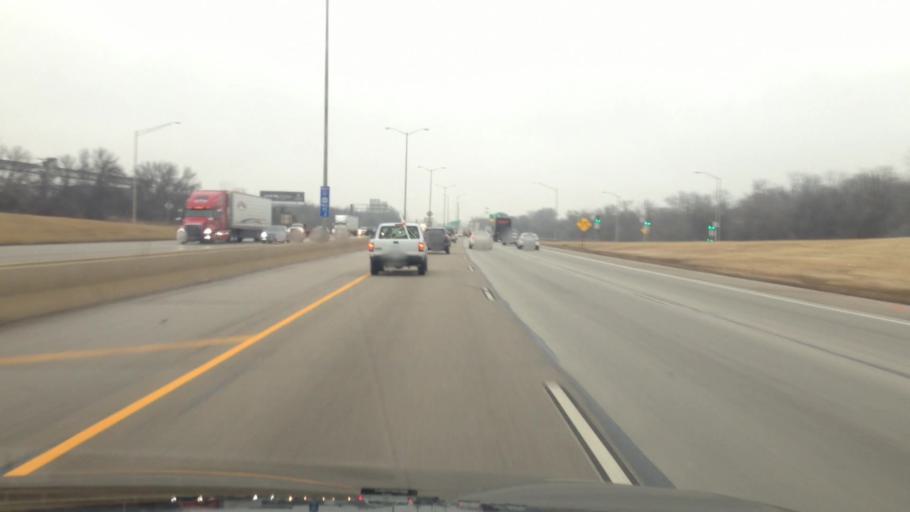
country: US
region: Wisconsin
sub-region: Waukesha County
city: Butler
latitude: 43.1055
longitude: -88.0579
